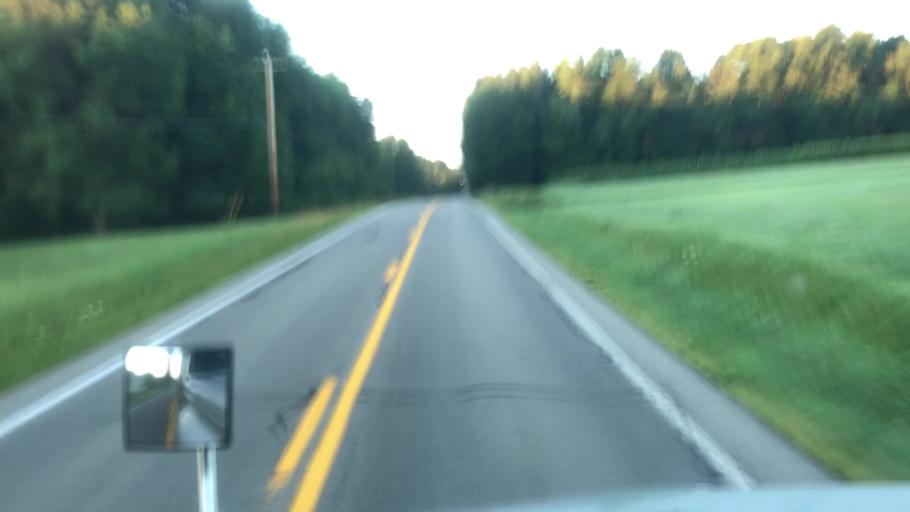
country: US
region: Pennsylvania
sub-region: Crawford County
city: Titusville
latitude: 41.5817
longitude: -79.6097
